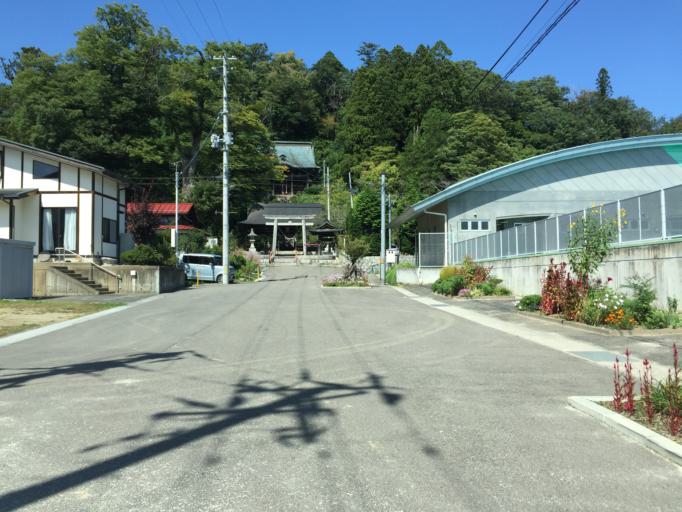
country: JP
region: Fukushima
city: Fukushima-shi
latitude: 37.6682
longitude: 140.5983
